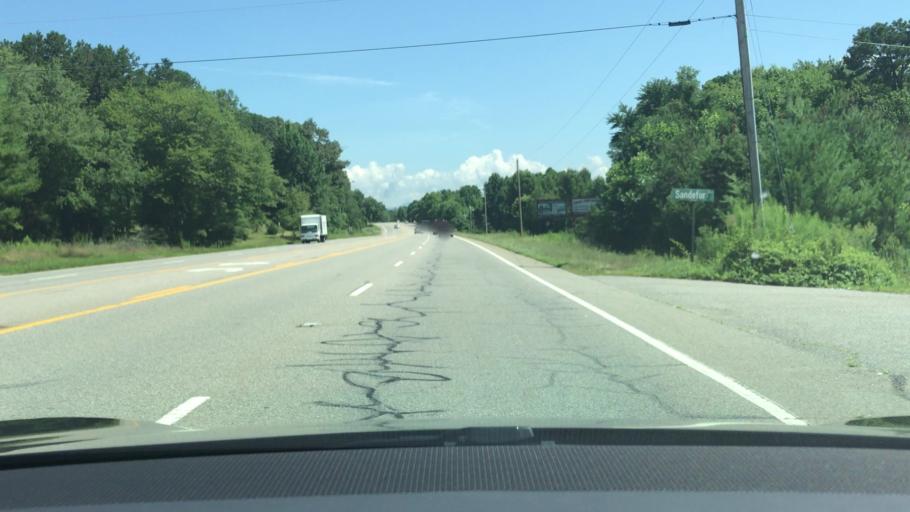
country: US
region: North Carolina
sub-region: Macon County
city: Franklin
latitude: 35.0730
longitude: -83.3863
